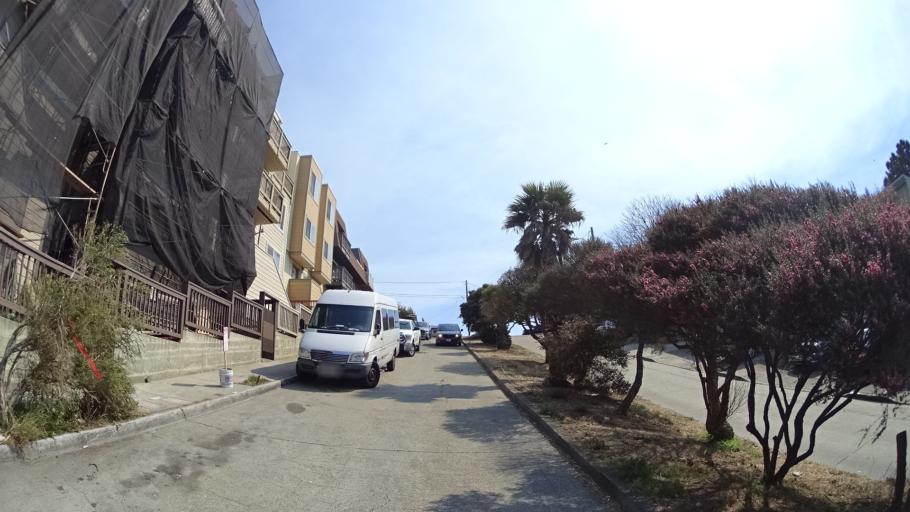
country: US
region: California
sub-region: San Mateo County
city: Daly City
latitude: 37.7158
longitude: -122.4543
